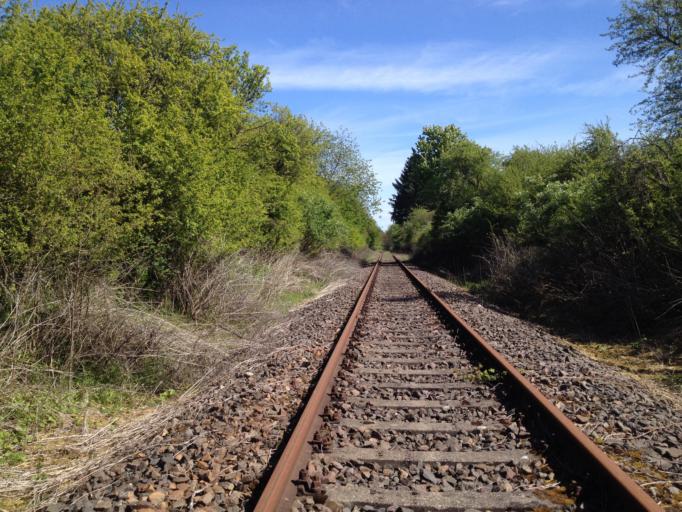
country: DE
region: Brandenburg
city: Templin
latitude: 53.1162
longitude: 13.4580
